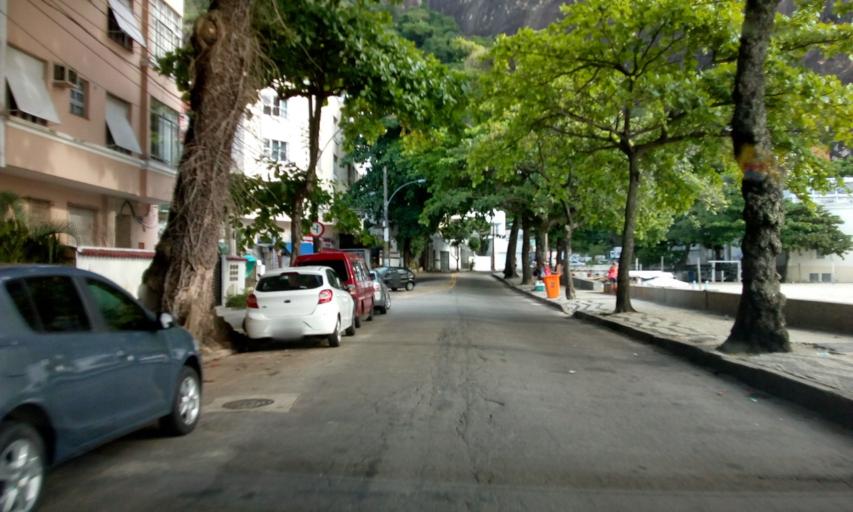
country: BR
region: Rio de Janeiro
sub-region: Rio De Janeiro
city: Rio de Janeiro
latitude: -22.9473
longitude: -43.1630
